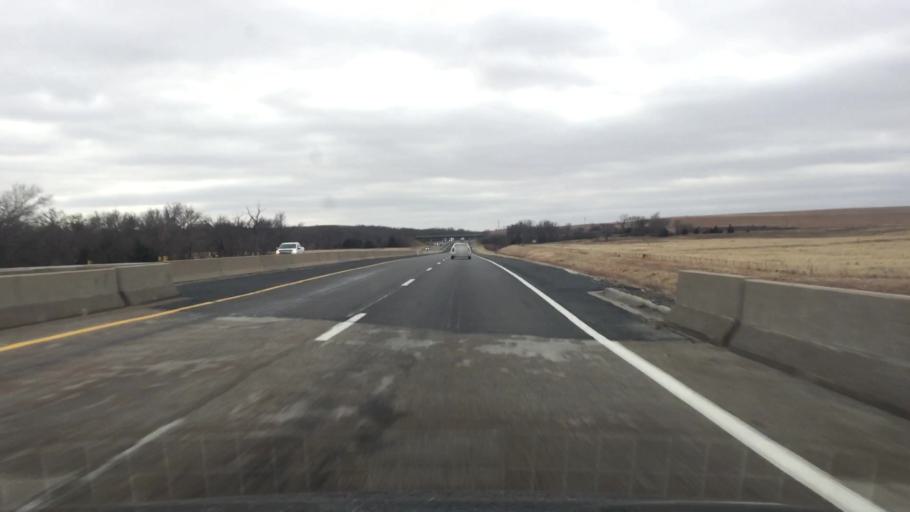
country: US
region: Kansas
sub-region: Chase County
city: Cottonwood Falls
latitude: 38.1280
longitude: -96.5482
